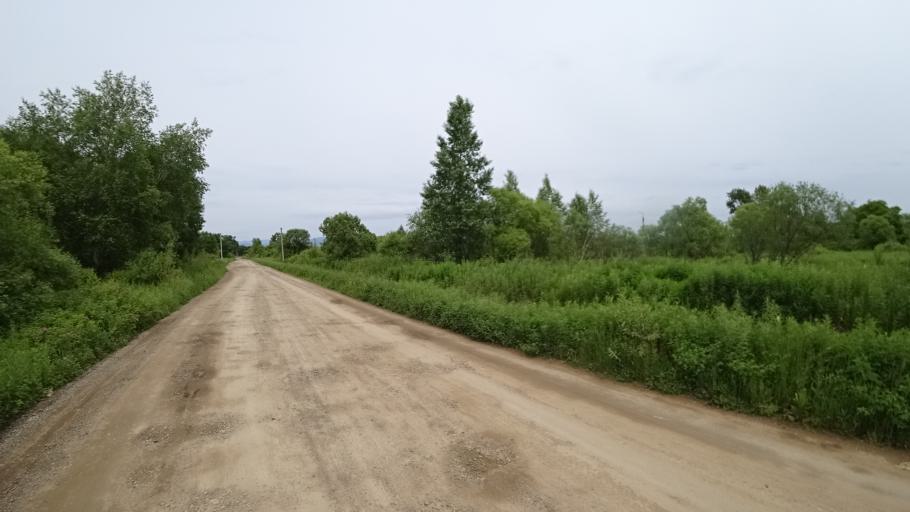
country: RU
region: Primorskiy
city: Arsen'yev
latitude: 44.1945
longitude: 133.3093
